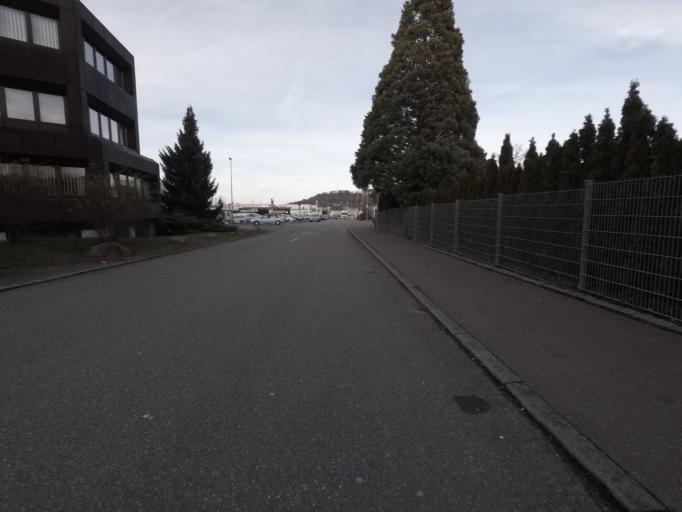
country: DE
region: Baden-Wuerttemberg
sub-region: Tuebingen Region
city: Pfullingen
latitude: 48.4741
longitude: 9.2264
